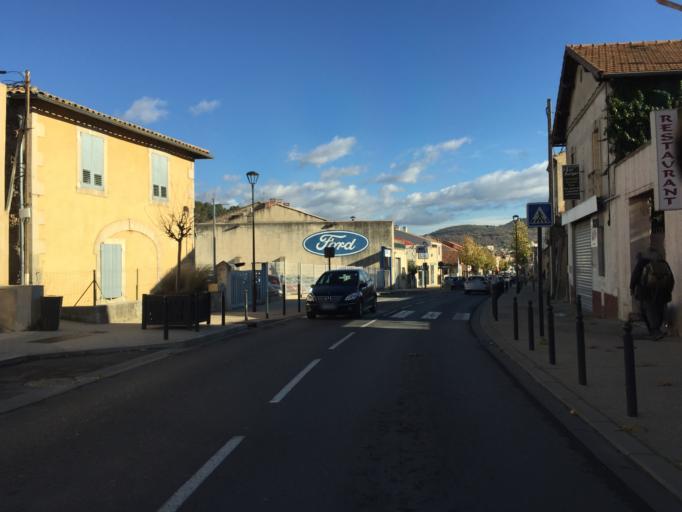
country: FR
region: Provence-Alpes-Cote d'Azur
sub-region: Departement du Vaucluse
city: Apt
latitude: 43.8783
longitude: 5.3877
